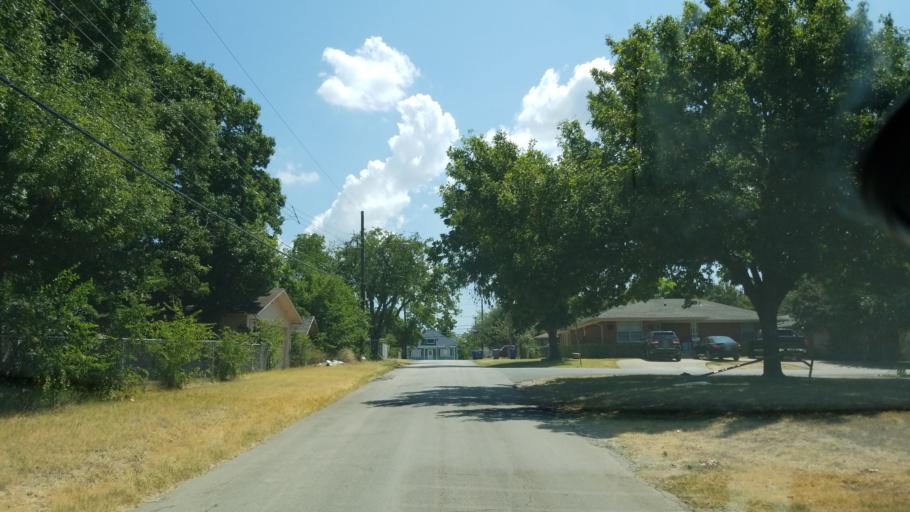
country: US
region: Texas
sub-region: Dallas County
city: Cockrell Hill
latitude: 32.7328
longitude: -96.8929
